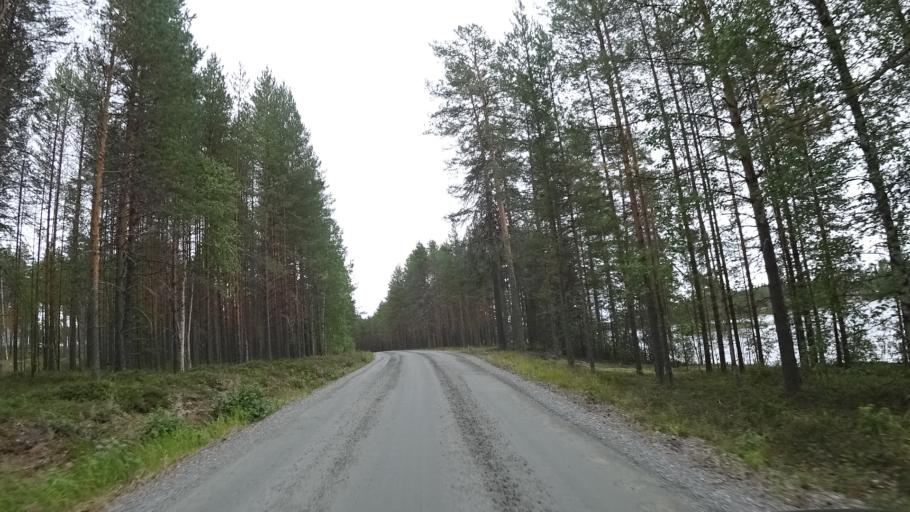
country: FI
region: North Karelia
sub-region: Pielisen Karjala
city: Lieksa
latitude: 63.3800
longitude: 30.3434
